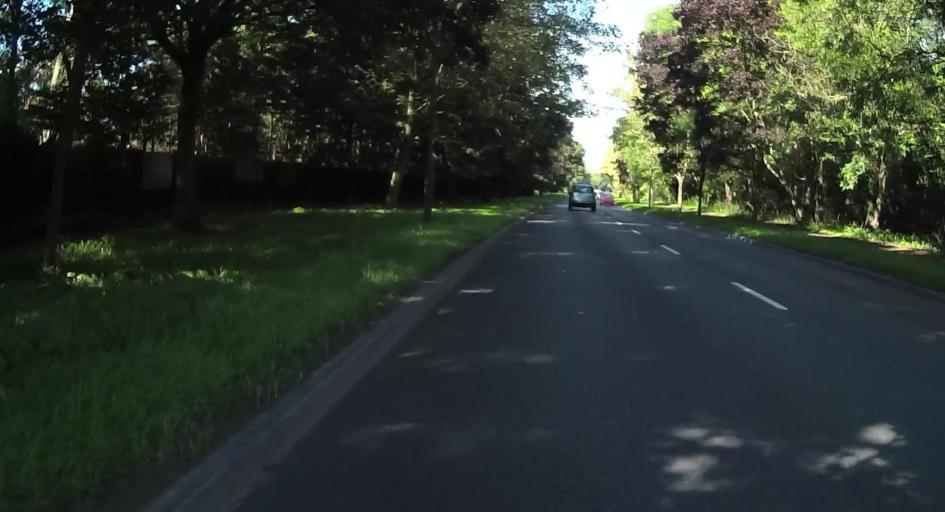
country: GB
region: England
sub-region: Surrey
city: Weybridge
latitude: 51.3725
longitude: -0.4704
